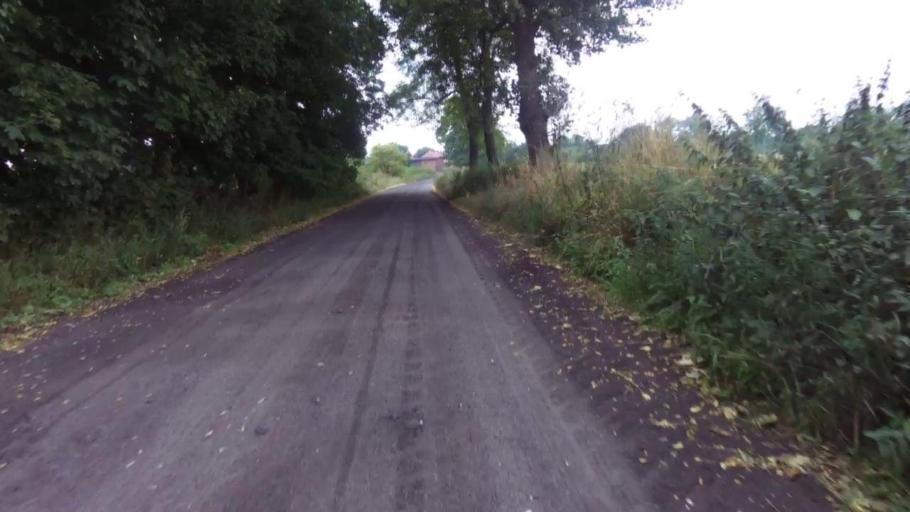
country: PL
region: West Pomeranian Voivodeship
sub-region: Powiat choszczenski
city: Choszczno
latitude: 53.2317
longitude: 15.3826
